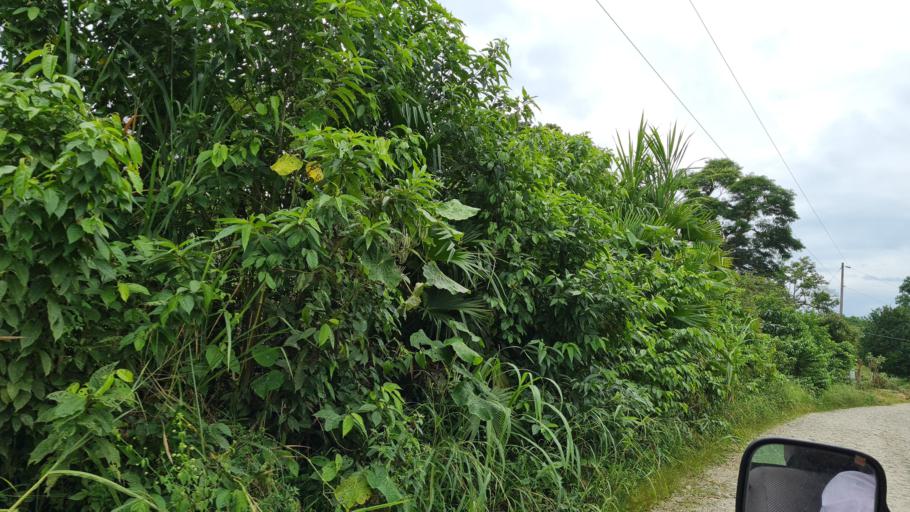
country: EC
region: Napo
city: Tena
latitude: -1.0031
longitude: -77.7689
